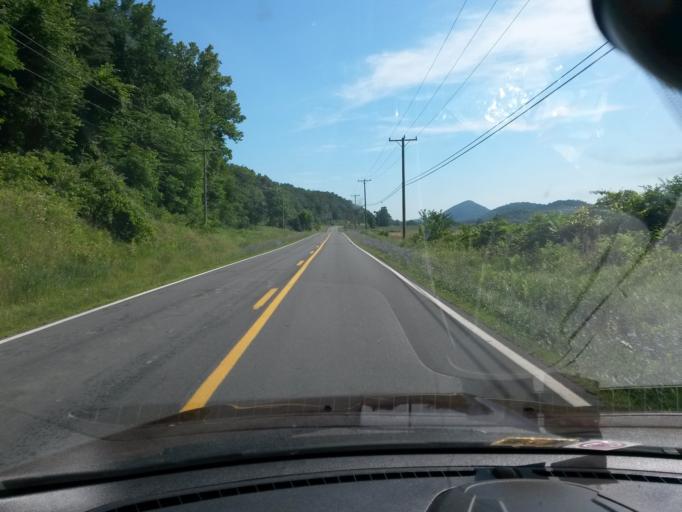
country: US
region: West Virginia
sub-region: Hardy County
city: Moorefield
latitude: 39.0299
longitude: -78.7544
